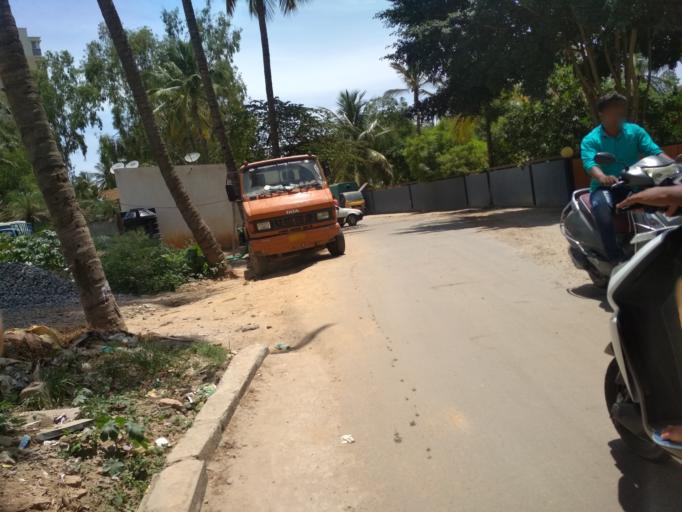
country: IN
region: Karnataka
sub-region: Bangalore Urban
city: Bangalore
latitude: 12.9298
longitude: 77.6721
